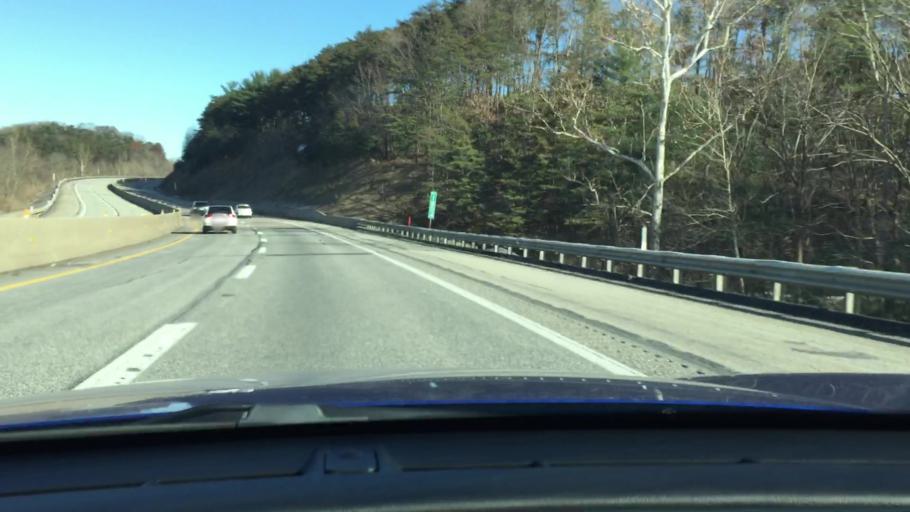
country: US
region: Pennsylvania
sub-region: Fulton County
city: McConnellsburg
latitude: 40.0599
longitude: -77.9485
